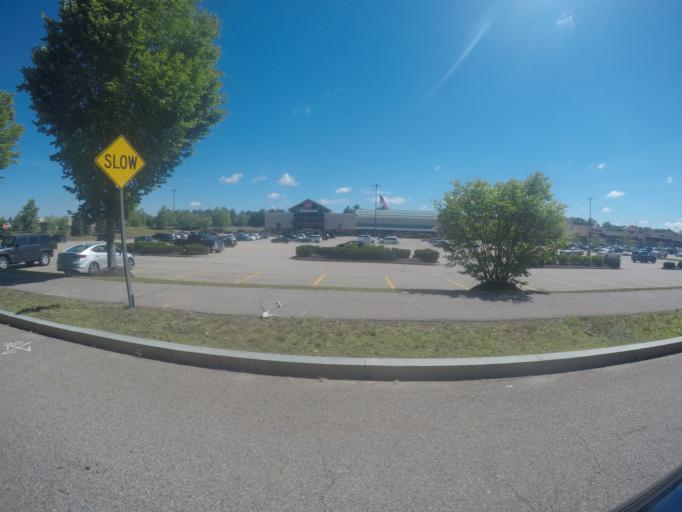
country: US
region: Massachusetts
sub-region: Bristol County
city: Easton
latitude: 42.0247
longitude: -71.1430
